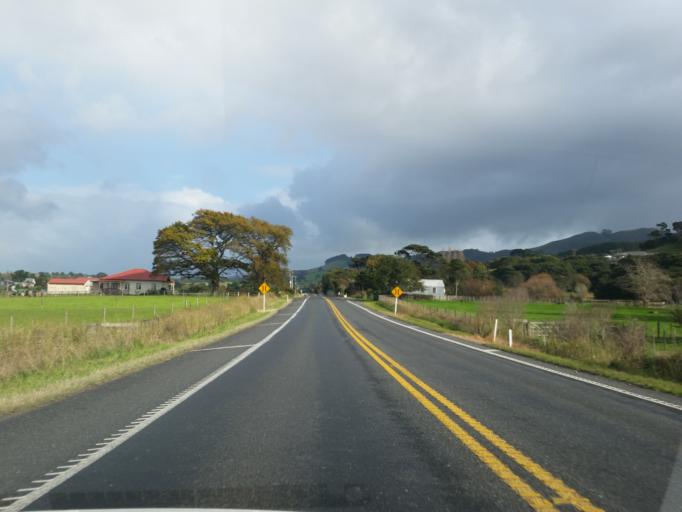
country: NZ
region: Auckland
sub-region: Auckland
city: Pukekohe East
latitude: -37.2152
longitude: 175.0638
